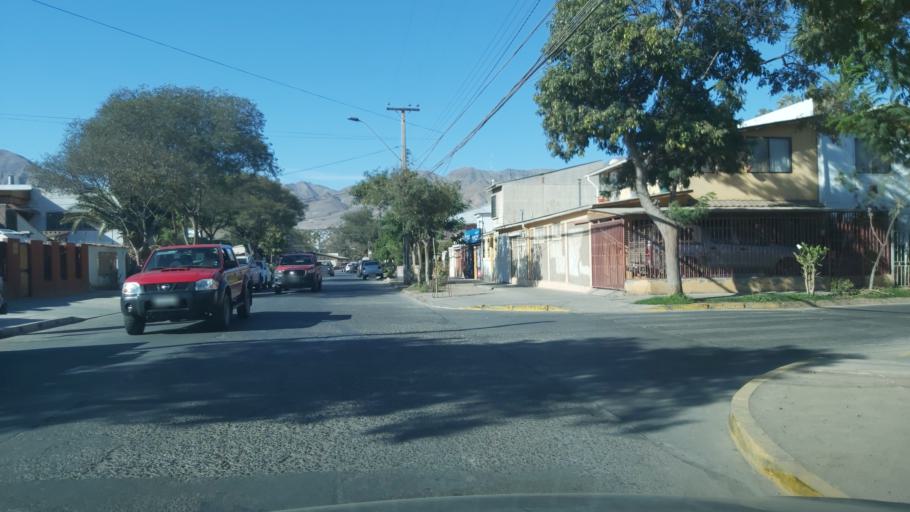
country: CL
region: Atacama
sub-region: Provincia de Copiapo
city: Copiapo
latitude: -27.3752
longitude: -70.3204
